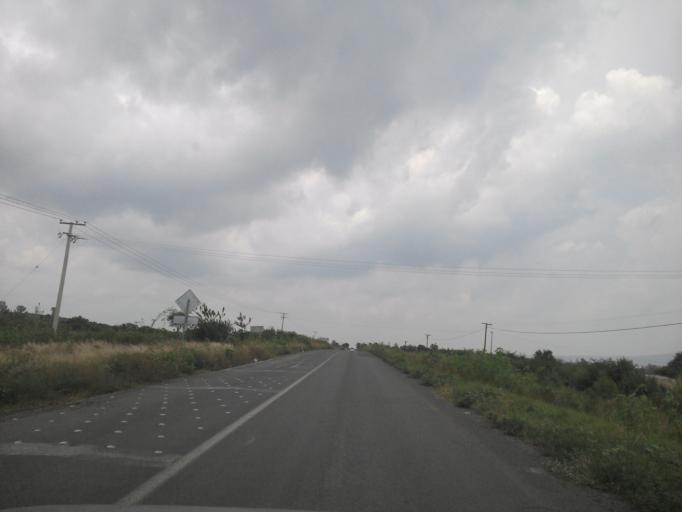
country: MX
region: Guanajuato
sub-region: San Francisco del Rincon
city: San Ignacio de Hidalgo
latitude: 20.8918
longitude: -101.9462
